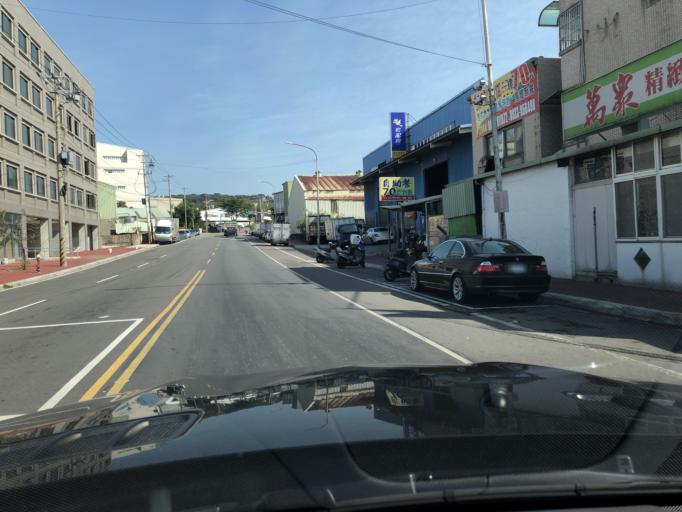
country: TW
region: Taiwan
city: Taoyuan City
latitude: 25.0733
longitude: 121.2854
